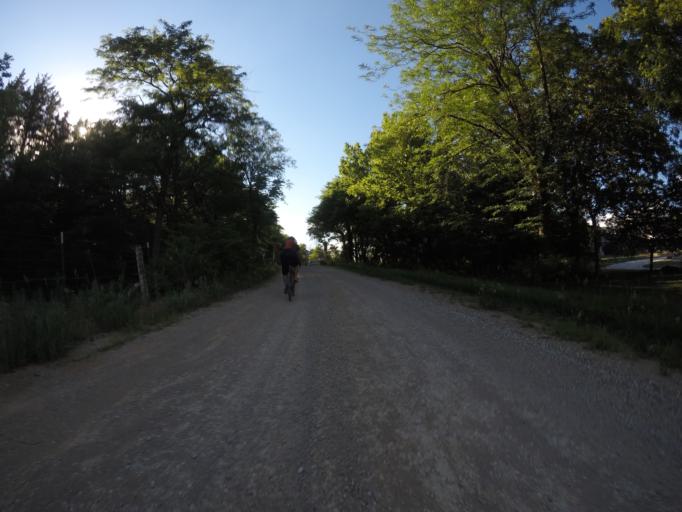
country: US
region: Kansas
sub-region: Riley County
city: Ogden
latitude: 39.2492
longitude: -96.7369
